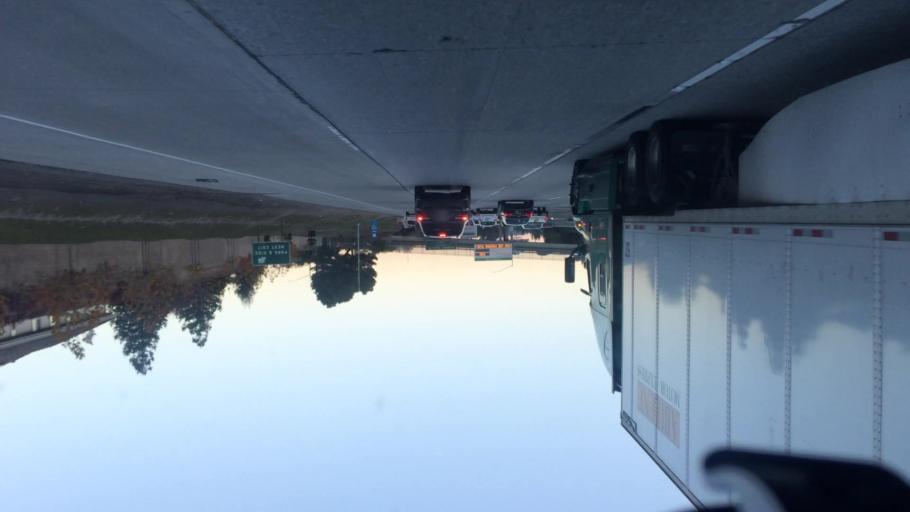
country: US
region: California
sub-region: Contra Costa County
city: San Ramon
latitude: 37.7907
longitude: -121.9821
